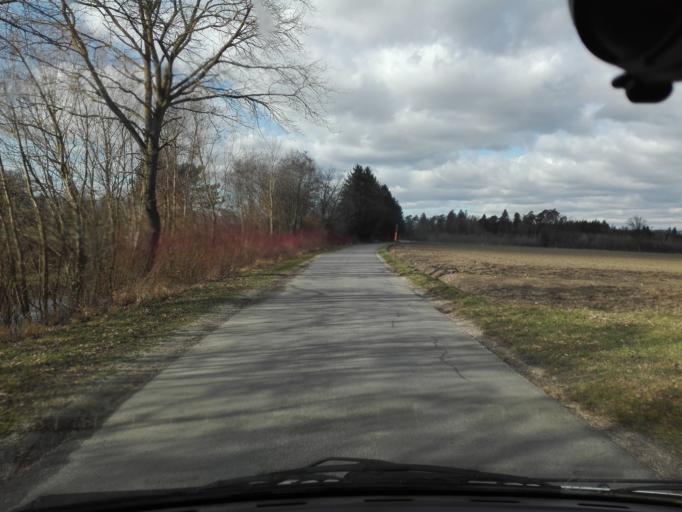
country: AT
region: Upper Austria
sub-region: Politischer Bezirk Perg
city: Perg
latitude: 48.2089
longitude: 14.6828
